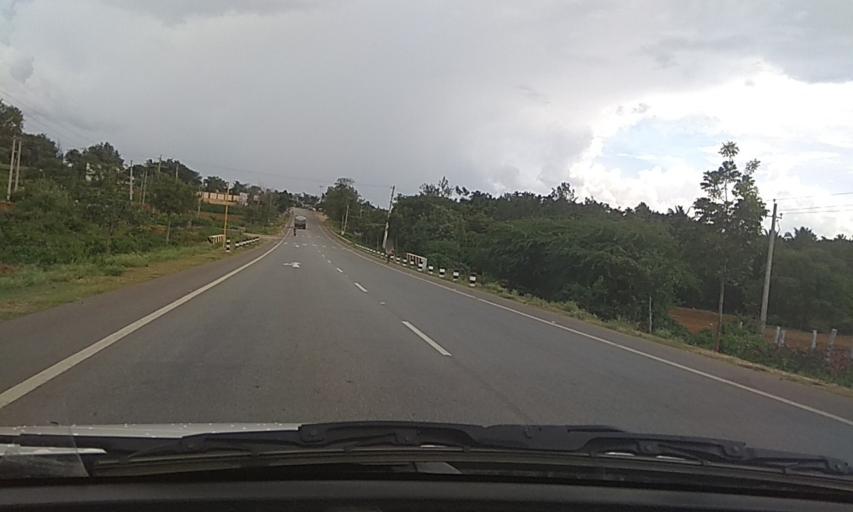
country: IN
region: Karnataka
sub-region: Tumkur
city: Kunigal
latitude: 12.8772
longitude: 77.0412
